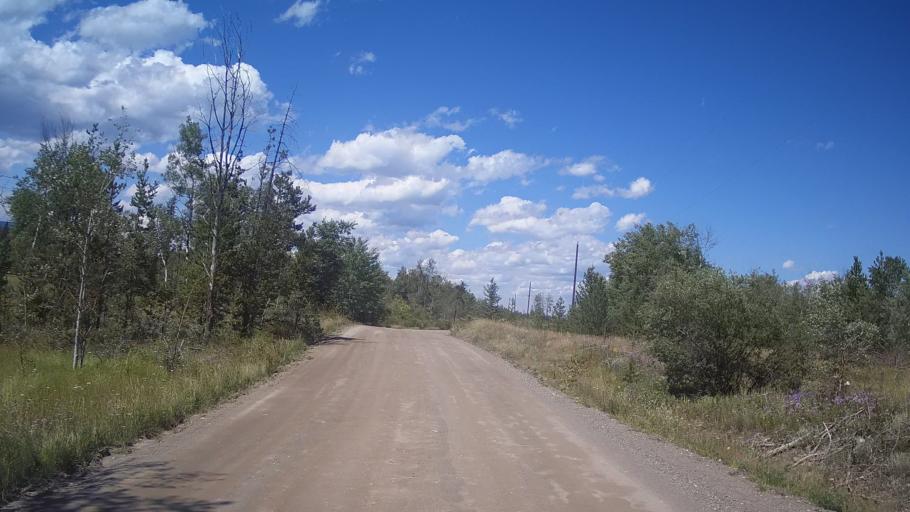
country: CA
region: British Columbia
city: Cache Creek
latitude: 51.2610
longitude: -121.6933
